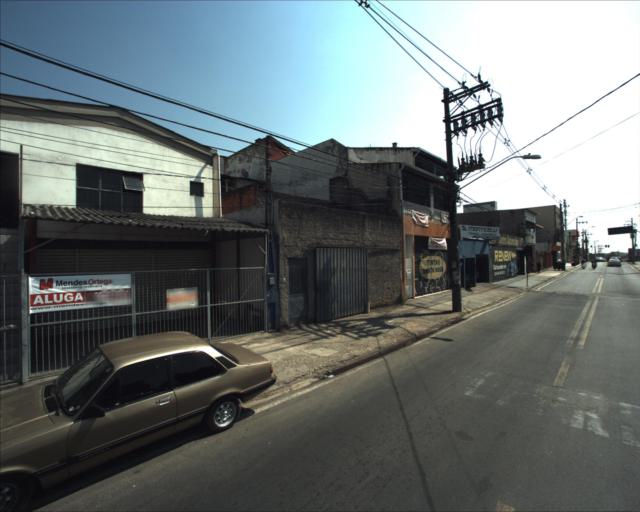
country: BR
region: Sao Paulo
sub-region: Sorocaba
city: Sorocaba
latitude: -23.4549
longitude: -47.4851
